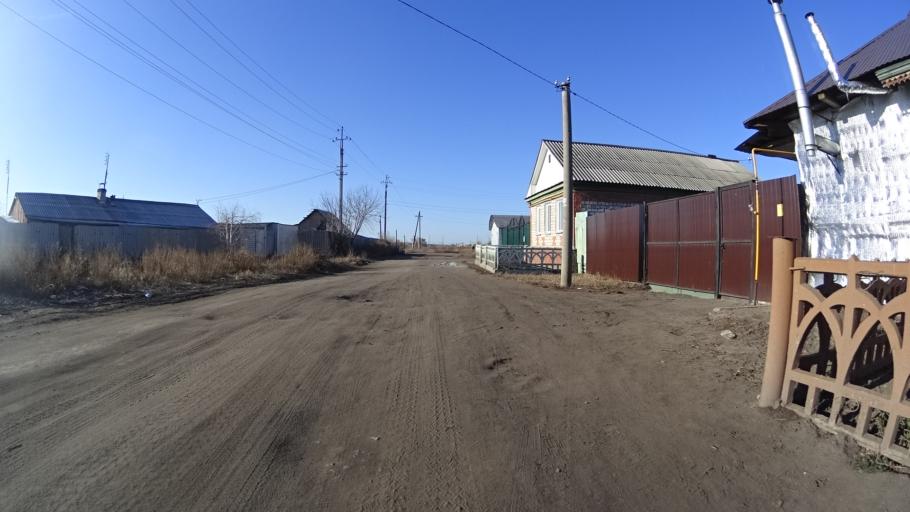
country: RU
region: Chelyabinsk
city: Troitsk
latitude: 54.0933
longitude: 61.5832
